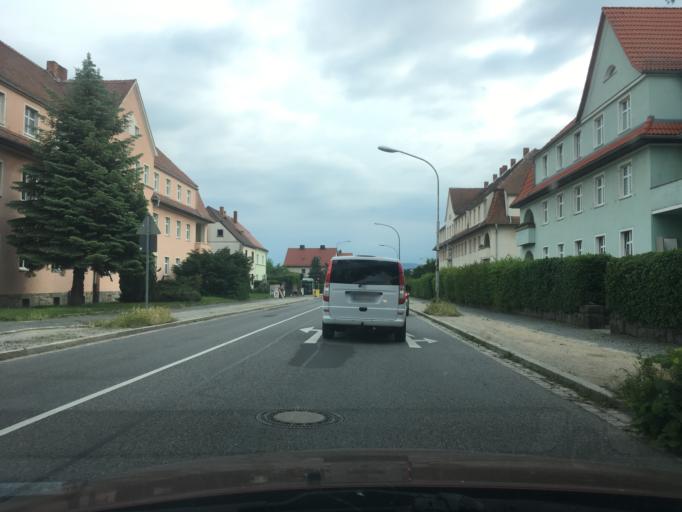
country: DE
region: Saxony
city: Bautzen
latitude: 51.1780
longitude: 14.4472
